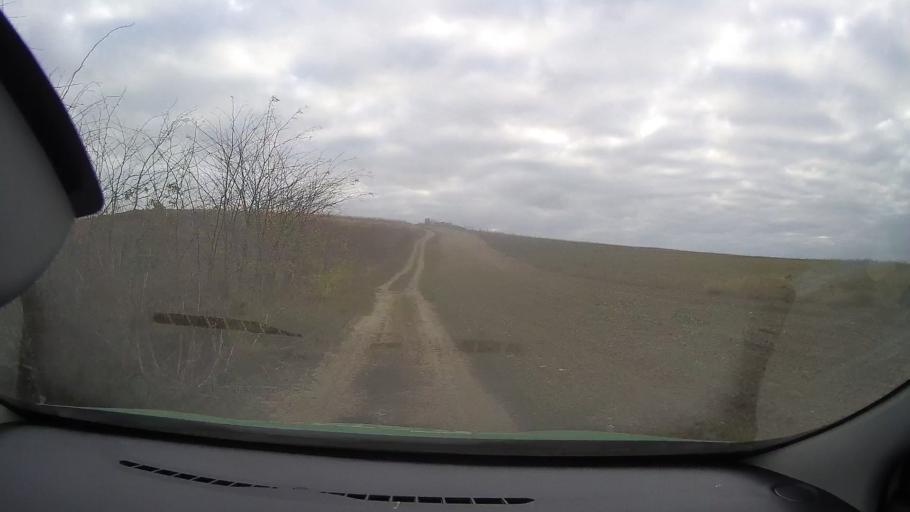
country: RO
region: Tulcea
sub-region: Comuna Jurilovca
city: Jurilovca
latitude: 44.7687
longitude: 28.9143
